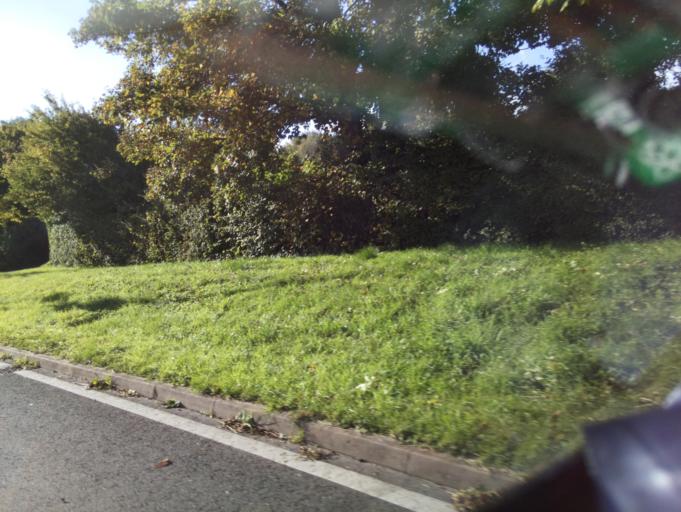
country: GB
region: Wales
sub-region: Sir Powys
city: Hay
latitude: 52.0056
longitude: -3.2541
